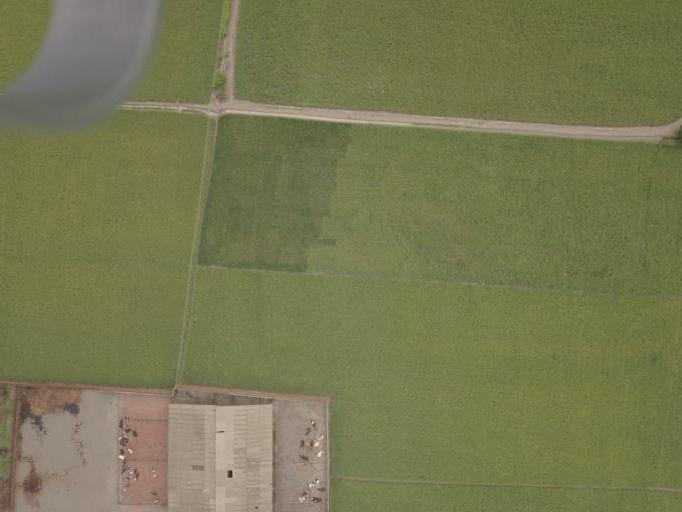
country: IN
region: Punjab
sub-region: Shahid Bhagat Singh Nagar
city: Rahon
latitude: 31.0176
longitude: 76.0945
